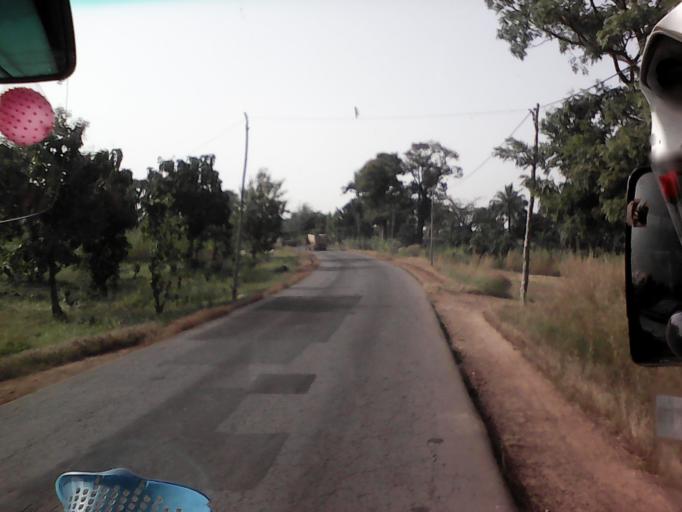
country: TG
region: Kara
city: Kara
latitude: 9.4867
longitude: 1.2084
